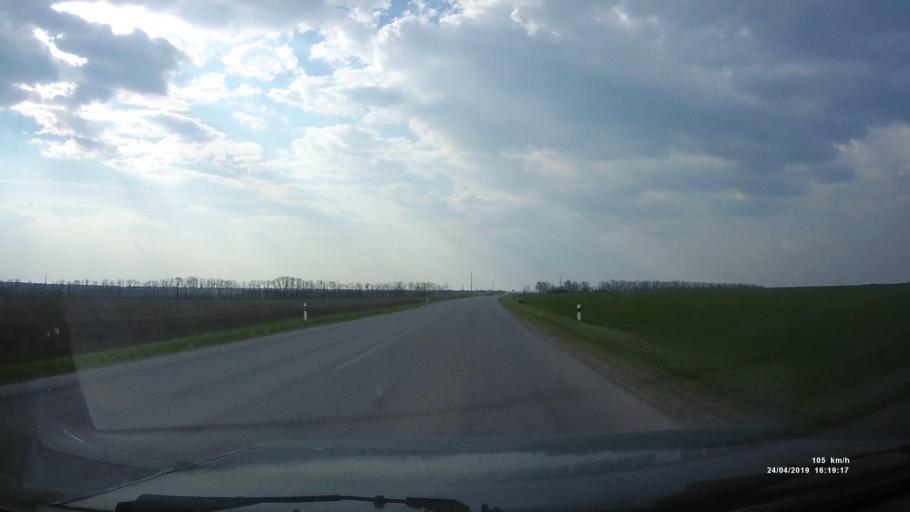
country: RU
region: Rostov
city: Sovetskoye
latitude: 46.7801
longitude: 42.0986
